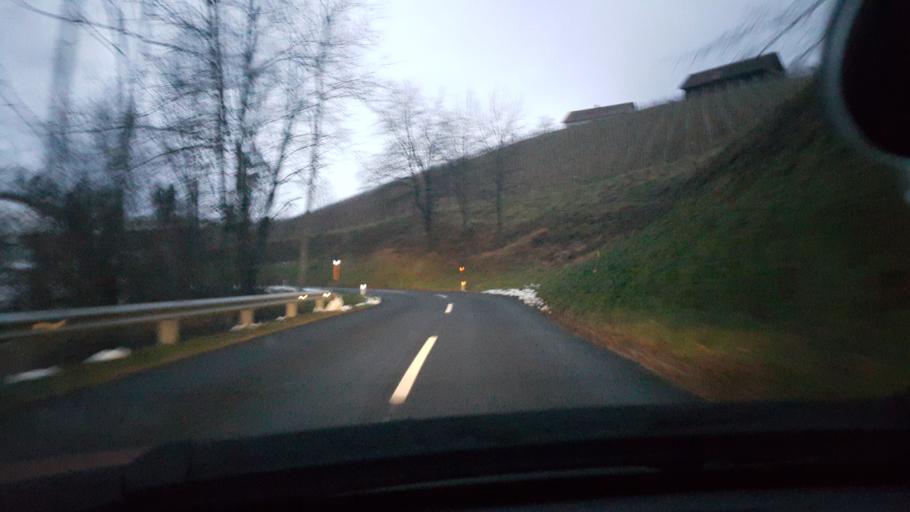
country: AT
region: Styria
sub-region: Politischer Bezirk Leibnitz
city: Sulztal an der Weinstrasse
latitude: 46.6458
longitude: 15.5204
